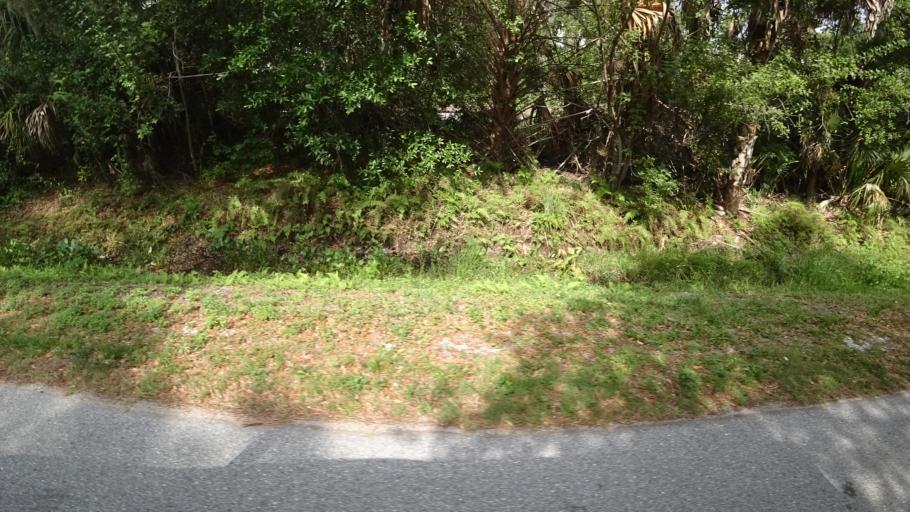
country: US
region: Florida
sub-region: Sarasota County
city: North Sarasota
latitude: 27.3995
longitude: -82.5301
